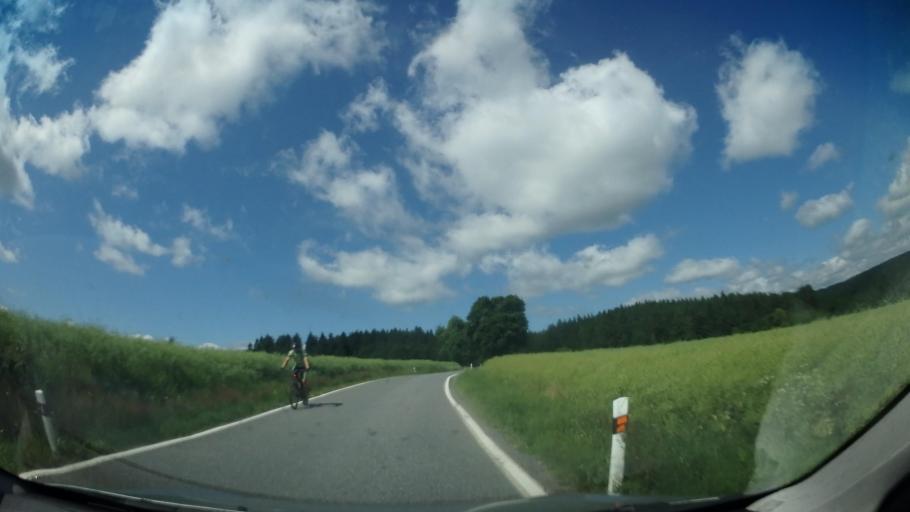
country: CZ
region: Vysocina
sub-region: Okres Zd'ar nad Sazavou
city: Nove Mesto na Morave
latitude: 49.6286
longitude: 16.0657
